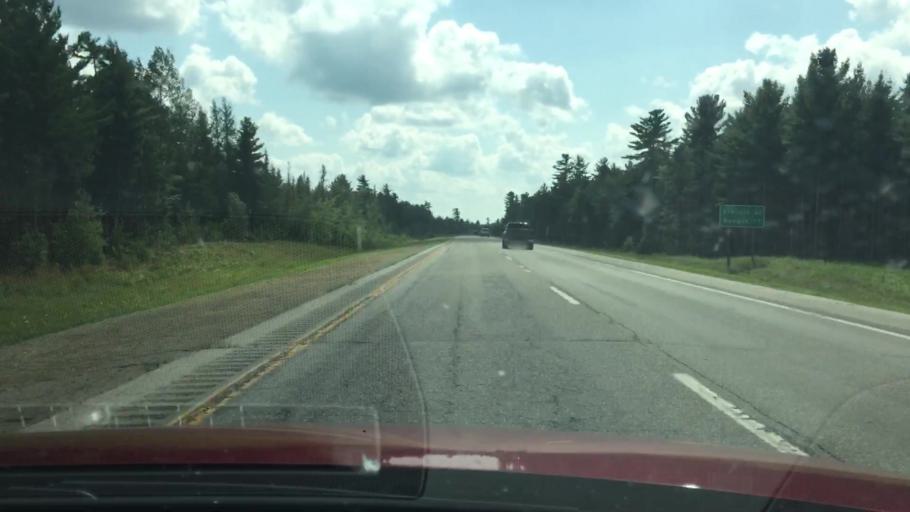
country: US
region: Maine
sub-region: Penobscot County
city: Medway
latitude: 45.5793
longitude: -68.5438
